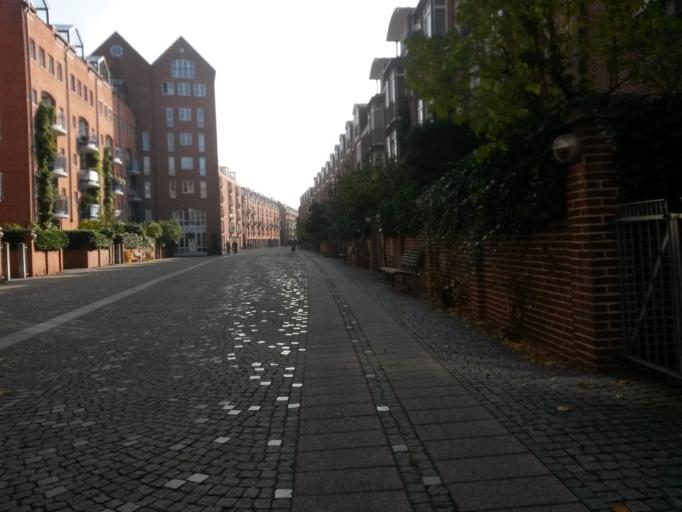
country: DE
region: Bremen
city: Bremen
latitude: 53.0763
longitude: 8.7994
